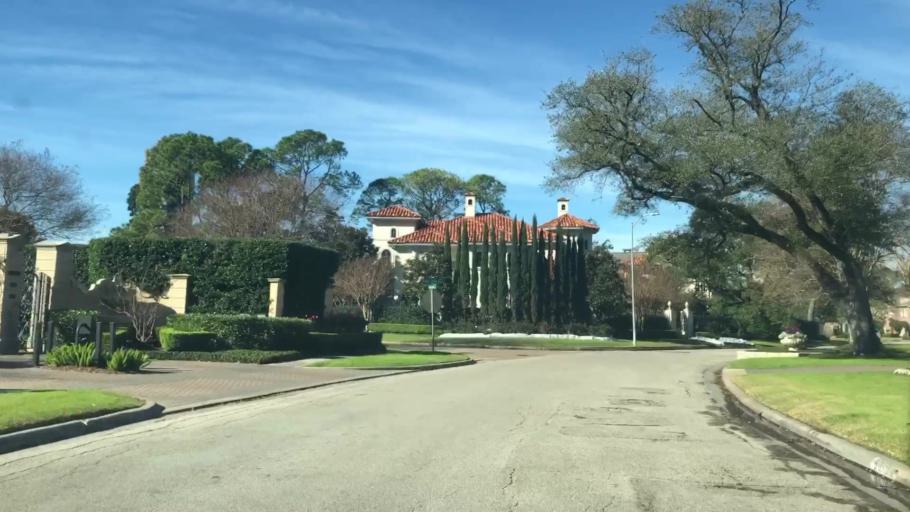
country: US
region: Texas
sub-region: Harris County
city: Hunters Creek Village
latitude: 29.7531
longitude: -95.4634
